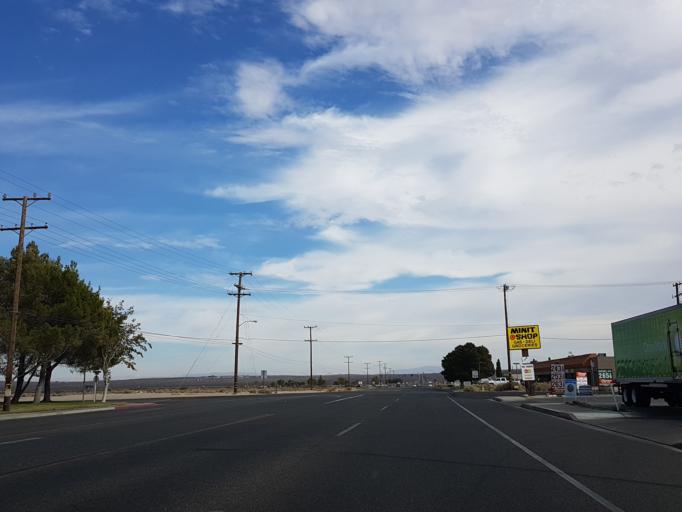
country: US
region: California
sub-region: Kern County
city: Ridgecrest
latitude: 35.6224
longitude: -117.6531
